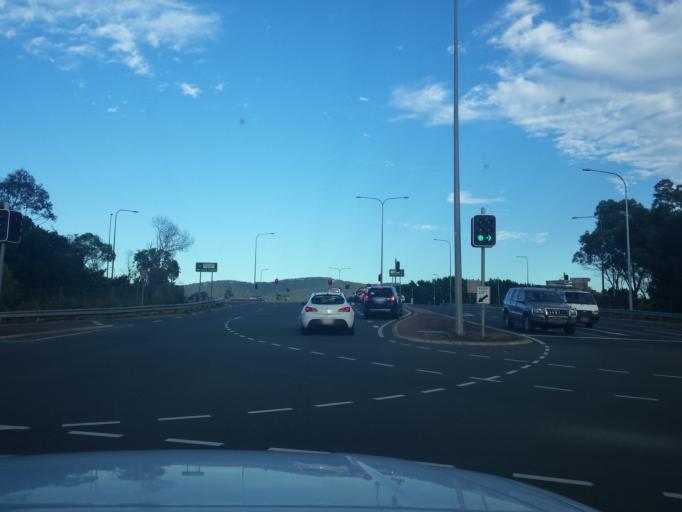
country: AU
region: Queensland
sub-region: Gold Coast
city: Oxenford
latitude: -27.8856
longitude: 153.3169
